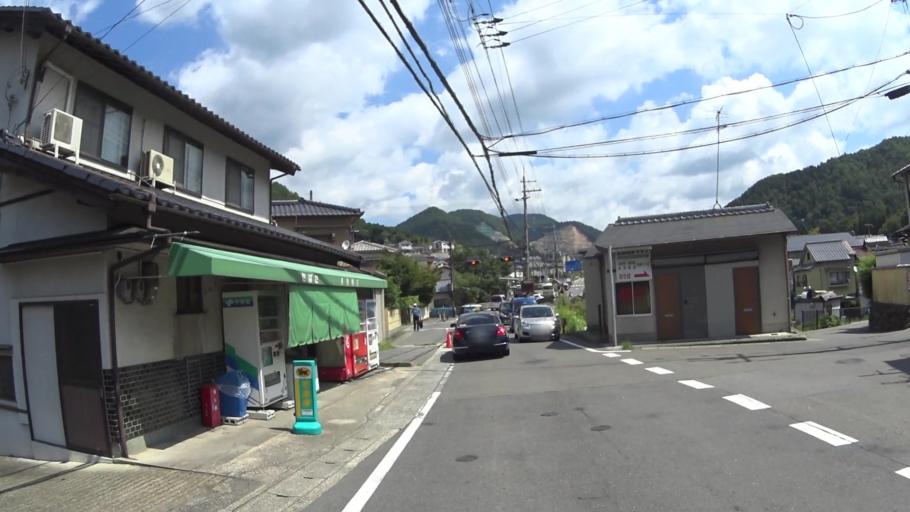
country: JP
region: Kyoto
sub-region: Kyoto-shi
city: Kamigyo-ku
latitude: 35.0882
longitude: 135.7623
